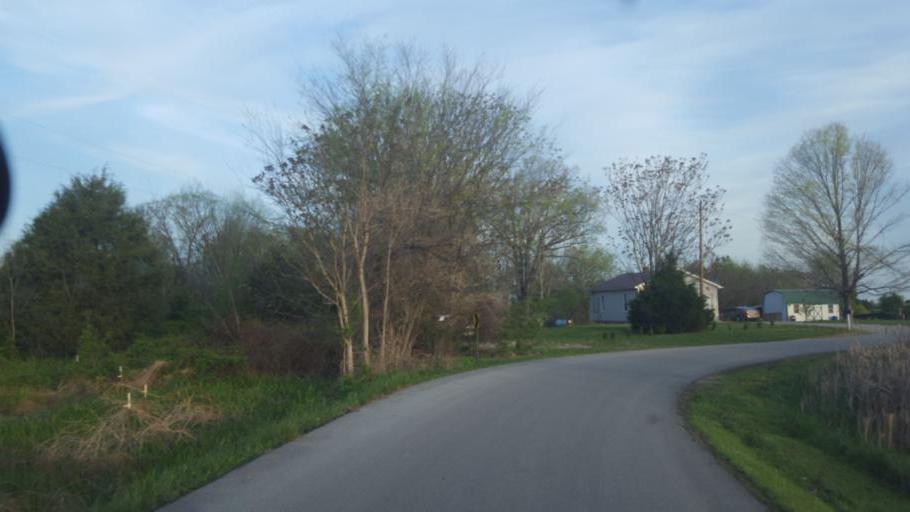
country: US
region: Kentucky
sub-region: Barren County
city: Cave City
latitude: 37.1561
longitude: -86.0113
